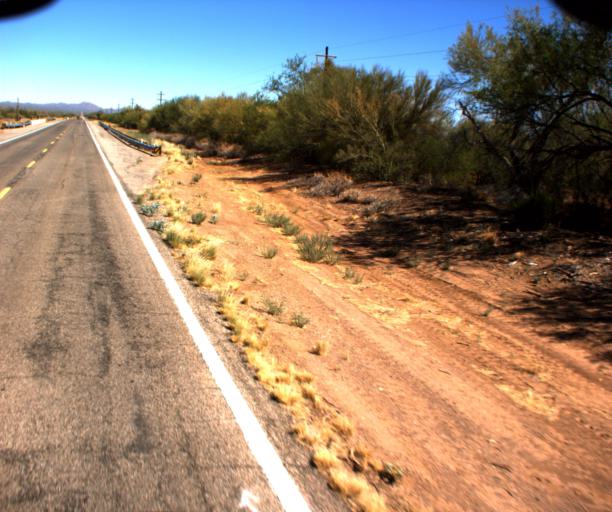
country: US
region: Arizona
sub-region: Pima County
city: Sells
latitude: 32.0581
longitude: -112.0318
